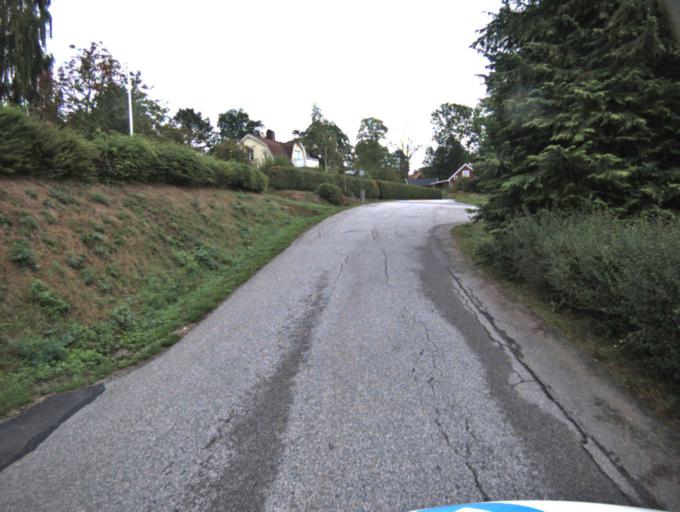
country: SE
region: Vaestra Goetaland
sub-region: Tranemo Kommun
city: Langhem
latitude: 57.6991
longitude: 13.3035
